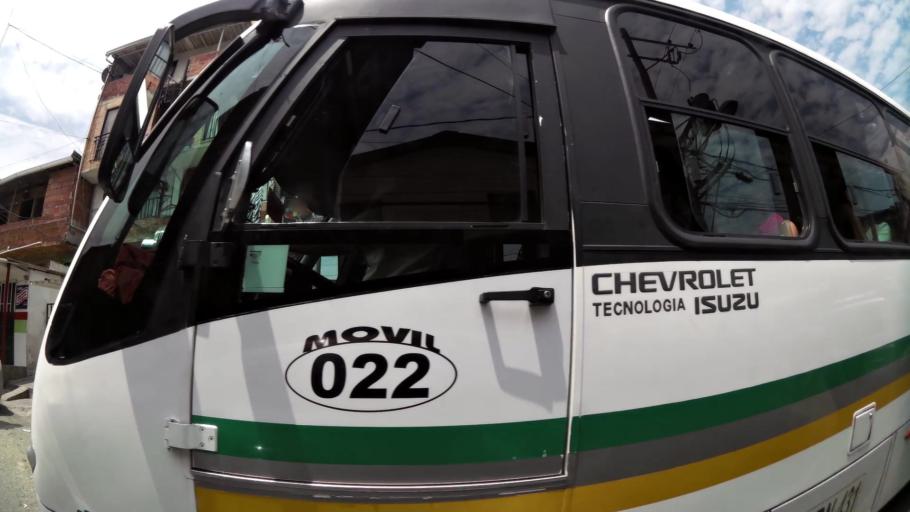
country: CO
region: Antioquia
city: Bello
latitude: 6.3120
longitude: -75.5784
